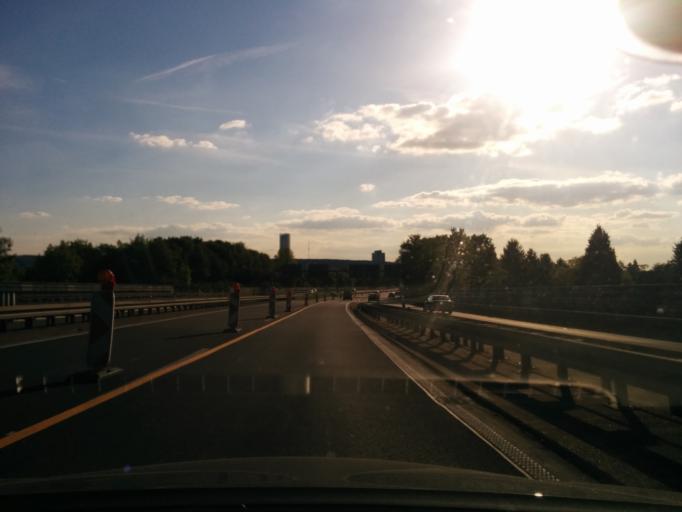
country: DE
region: North Rhine-Westphalia
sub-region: Regierungsbezirk Koln
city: Konigswinter
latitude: 50.7236
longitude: 7.1591
